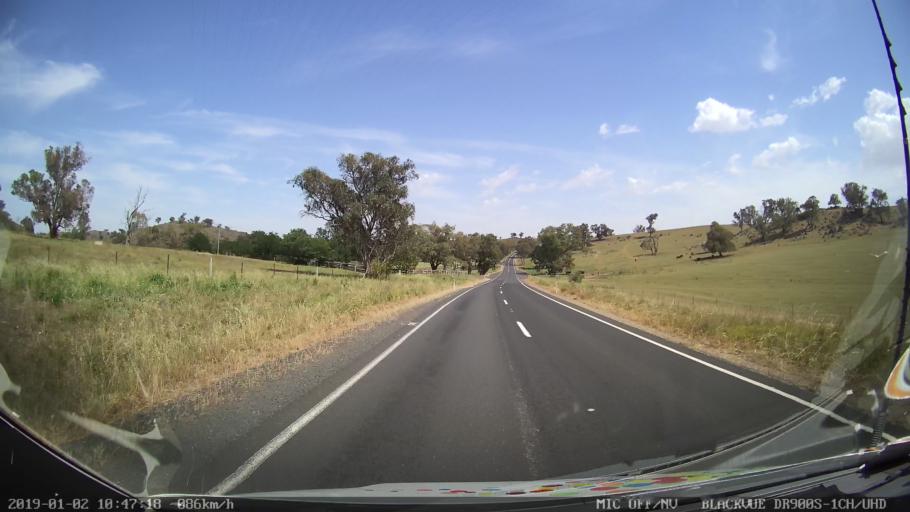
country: AU
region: New South Wales
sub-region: Cootamundra
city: Cootamundra
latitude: -34.7464
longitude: 148.2748
